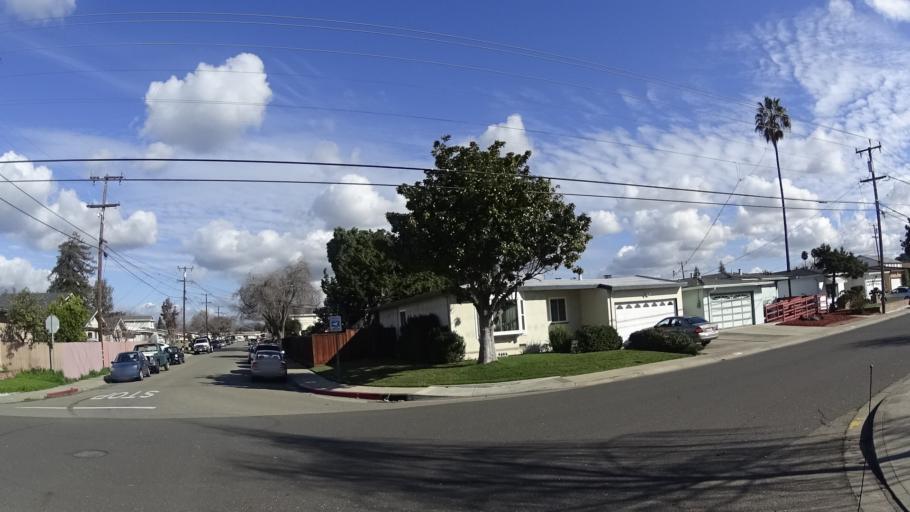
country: US
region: California
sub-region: Alameda County
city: San Lorenzo
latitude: 37.6723
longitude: -122.1173
